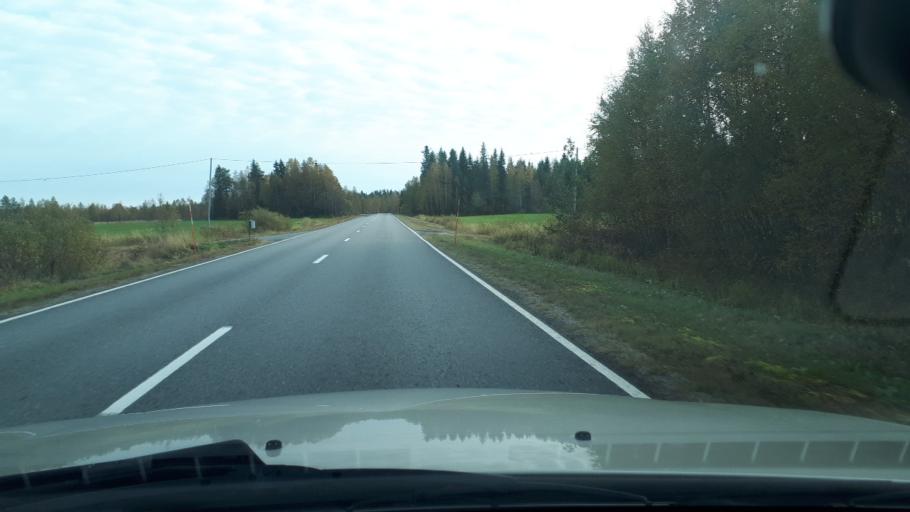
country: FI
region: Lapland
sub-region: Rovaniemi
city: Ranua
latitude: 65.9611
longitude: 26.0548
